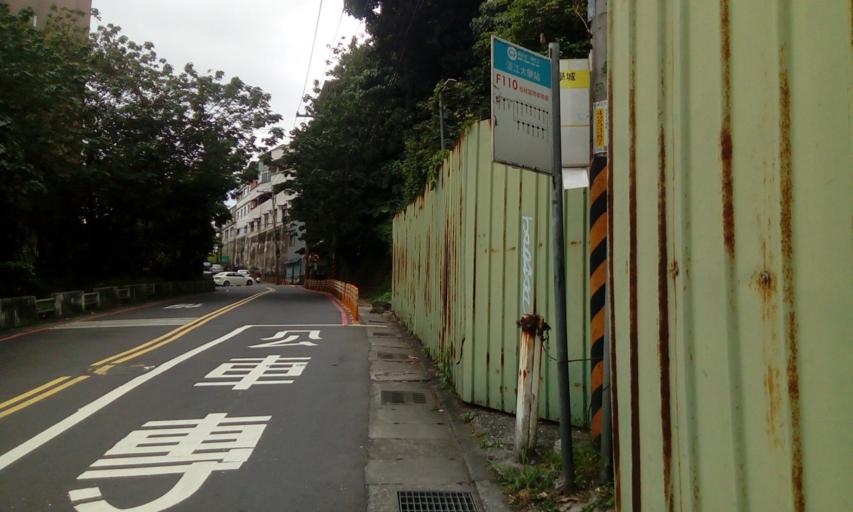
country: TW
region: Taipei
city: Taipei
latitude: 25.1732
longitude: 121.4503
